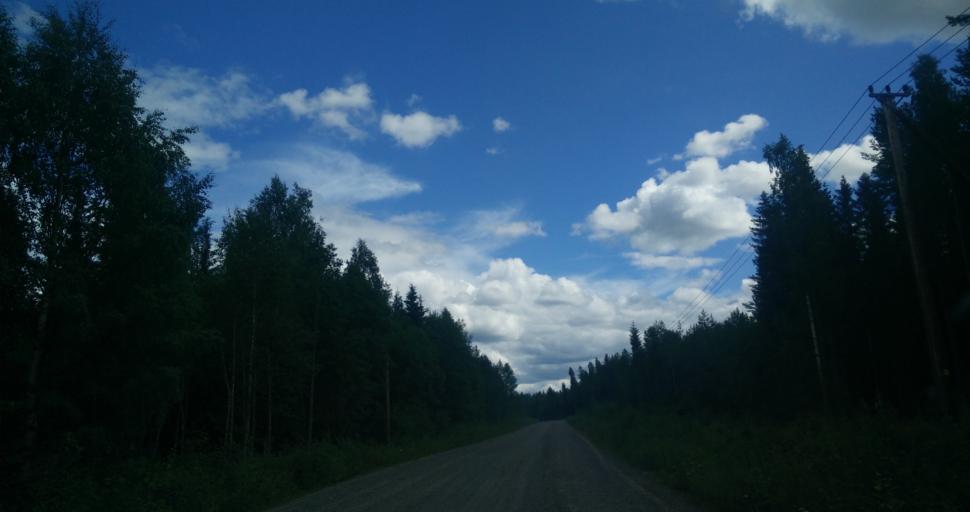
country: SE
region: Gaevleborg
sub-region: Nordanstigs Kommun
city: Bergsjoe
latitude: 62.0571
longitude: 16.8147
